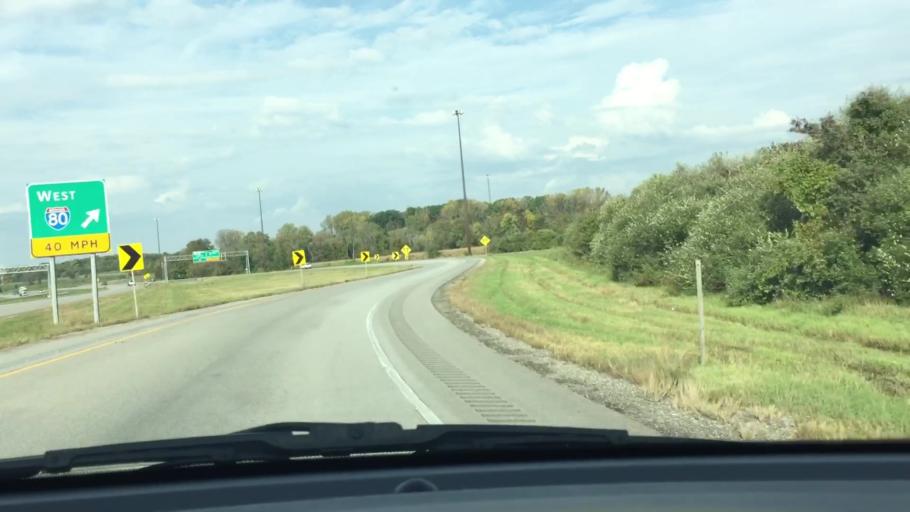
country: US
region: Illinois
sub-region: Henry County
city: Colona
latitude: 41.5367
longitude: -90.3296
